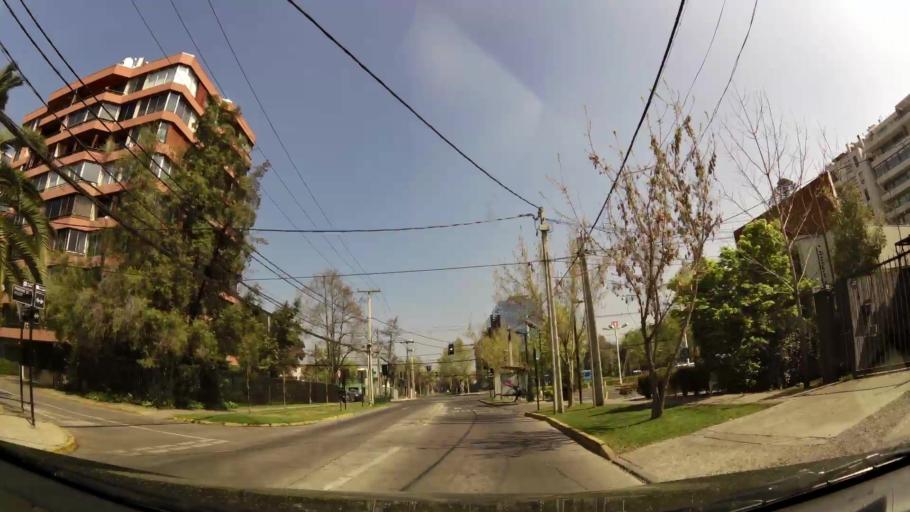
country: CL
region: Santiago Metropolitan
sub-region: Provincia de Santiago
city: Villa Presidente Frei, Nunoa, Santiago, Chile
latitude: -33.3919
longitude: -70.5922
